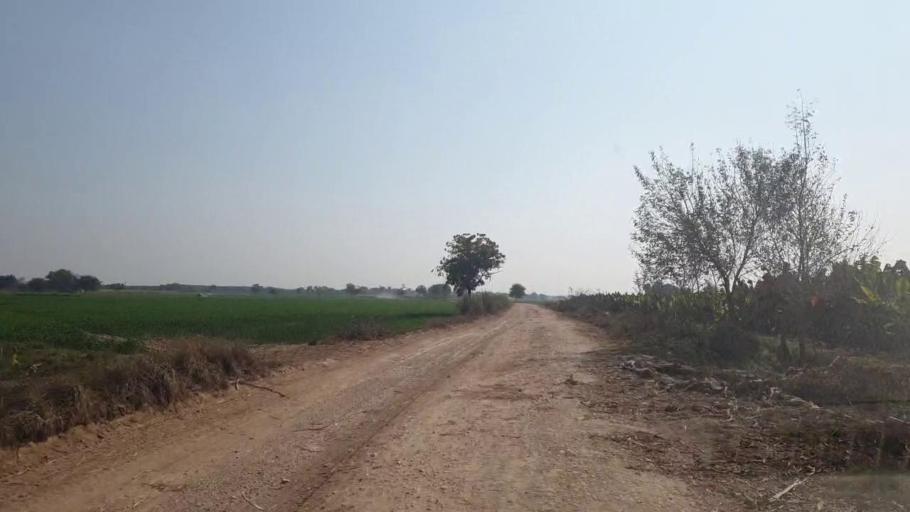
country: PK
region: Sindh
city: Sakrand
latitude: 26.0516
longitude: 68.4510
